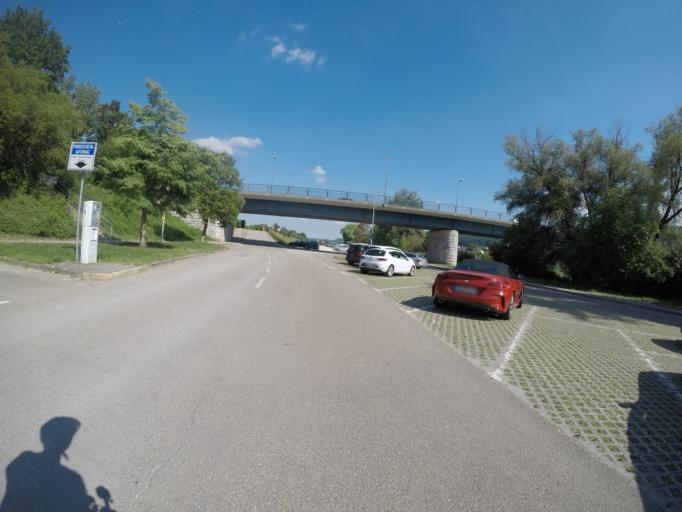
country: DE
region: Bavaria
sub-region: Lower Bavaria
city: Kelheim
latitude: 48.9143
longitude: 11.8729
